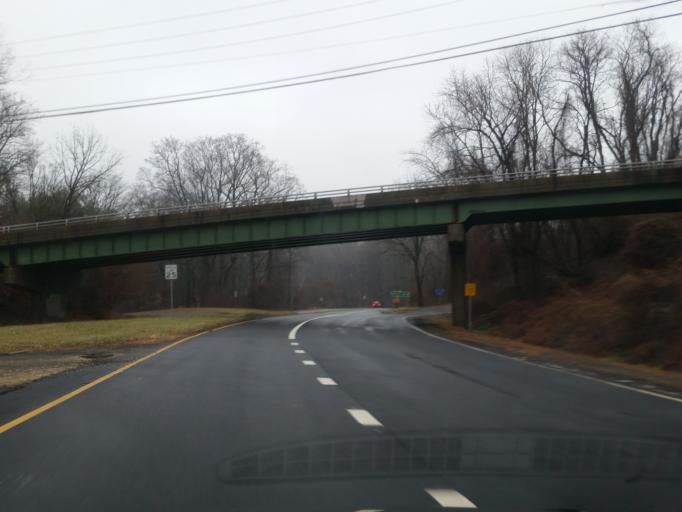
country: US
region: Maryland
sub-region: Montgomery County
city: Brookmont
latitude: 38.9260
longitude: -77.1227
